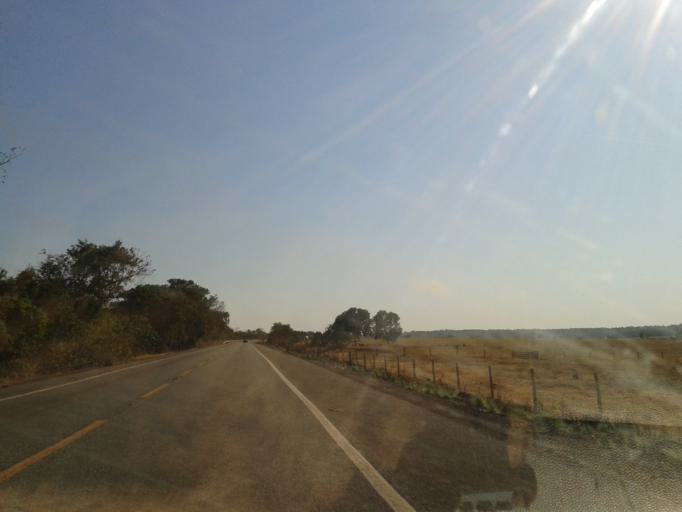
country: BR
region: Goias
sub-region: Mozarlandia
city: Mozarlandia
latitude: -14.8482
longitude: -50.5436
